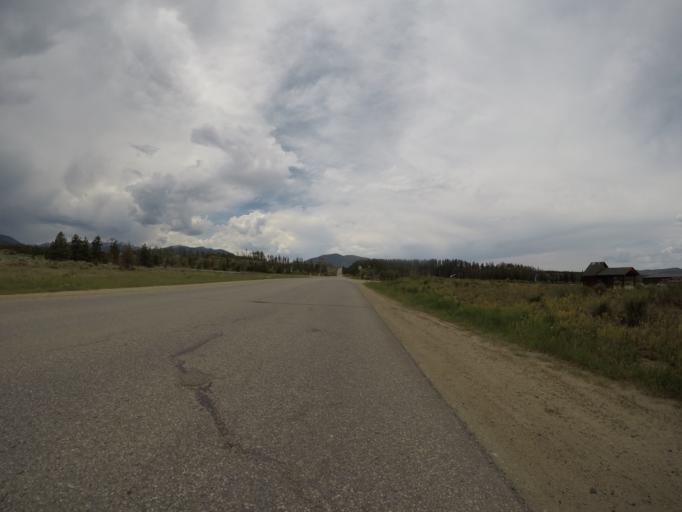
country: US
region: Colorado
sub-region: Grand County
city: Fraser
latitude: 39.9555
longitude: -105.8226
